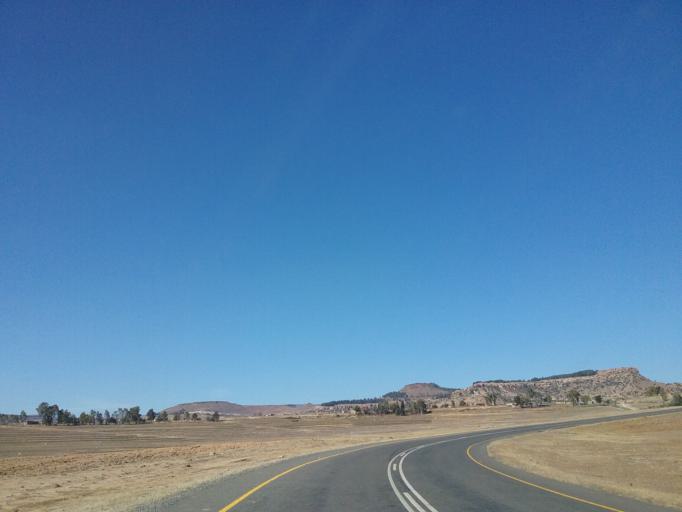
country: LS
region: Maseru
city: Nako
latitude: -29.4604
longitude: 27.6468
